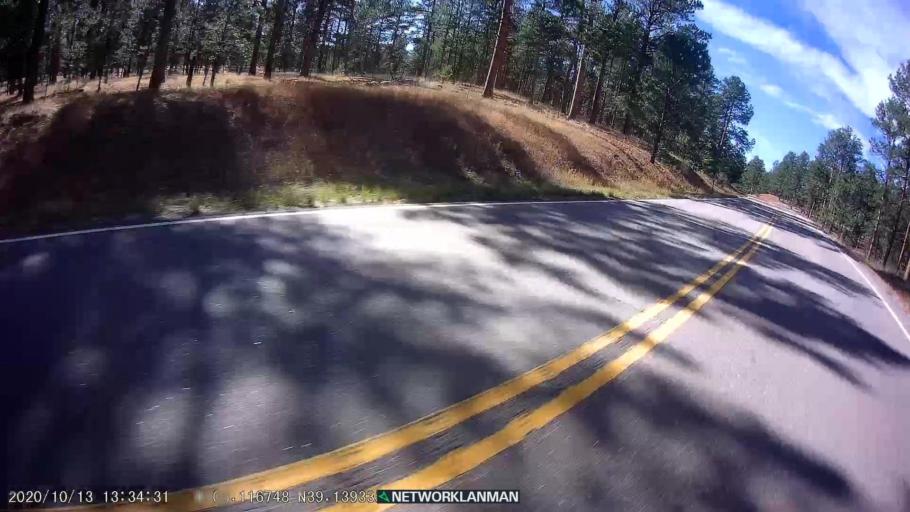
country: US
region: Colorado
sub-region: Teller County
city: Woodland Park
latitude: 39.1395
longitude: -105.1170
